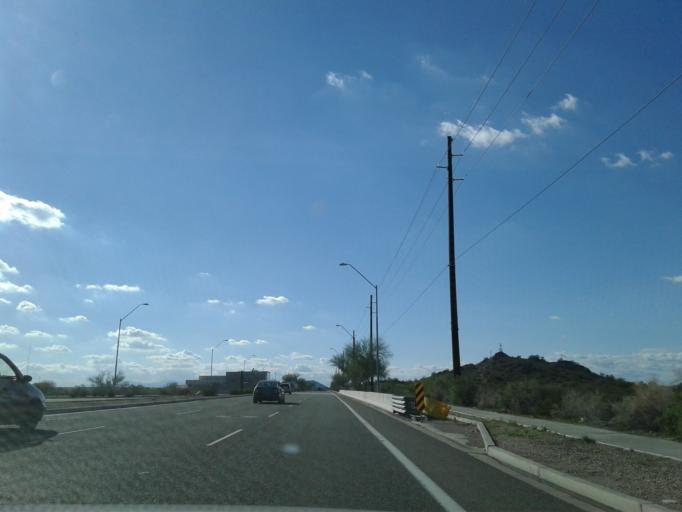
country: US
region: Arizona
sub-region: Maricopa County
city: Cave Creek
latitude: 33.6842
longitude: -112.0560
